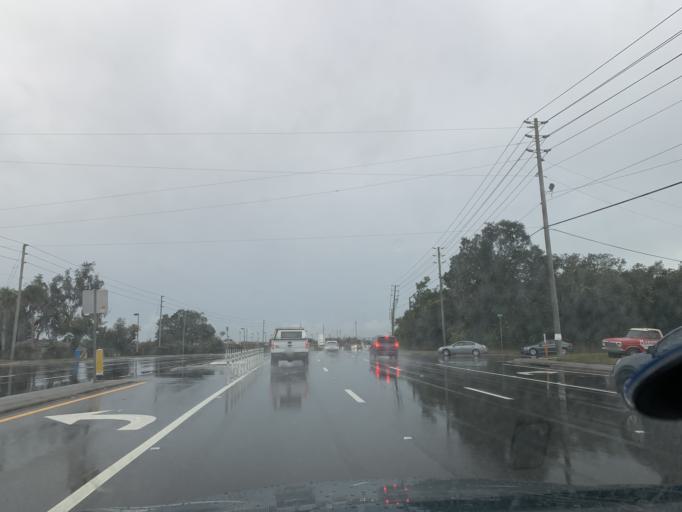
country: US
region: Florida
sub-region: Pasco County
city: Jasmine Estates
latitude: 28.3027
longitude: -82.6684
